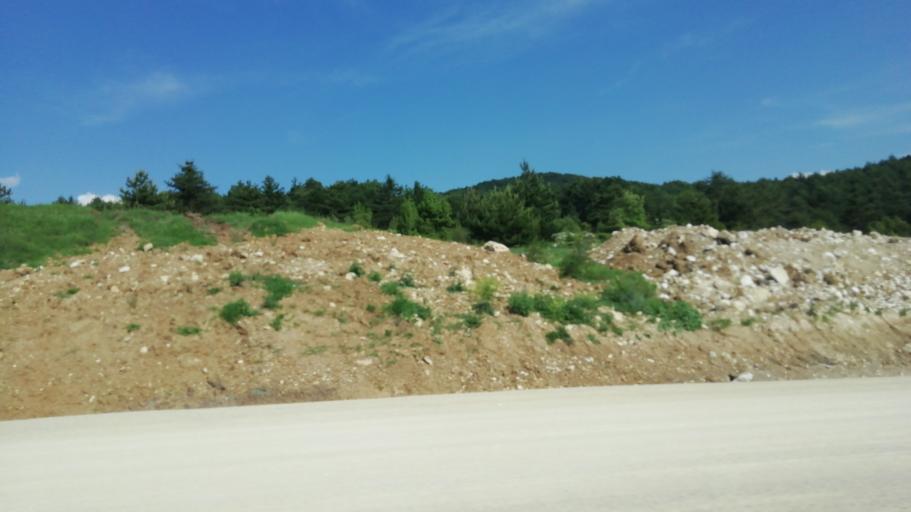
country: TR
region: Karabuk
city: Karabuk
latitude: 41.1195
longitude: 32.5809
